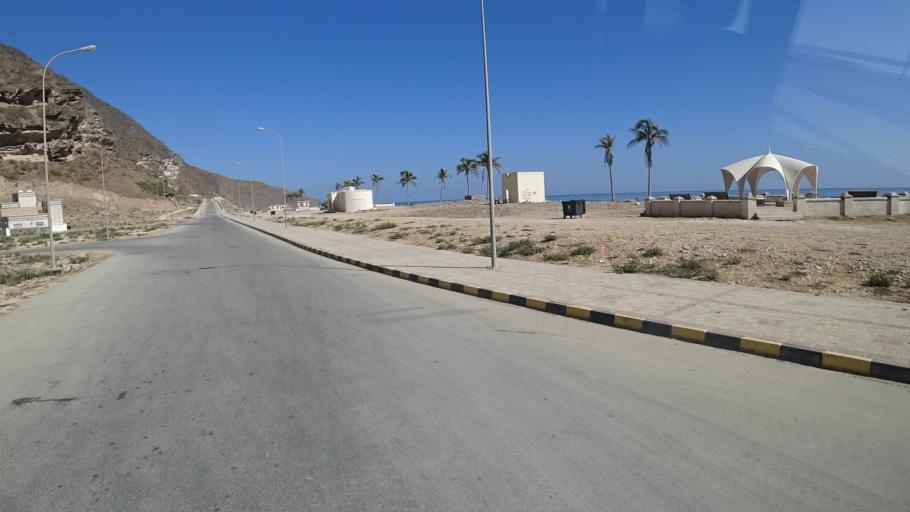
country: YE
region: Al Mahrah
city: Hawf
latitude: 16.7474
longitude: 53.4271
